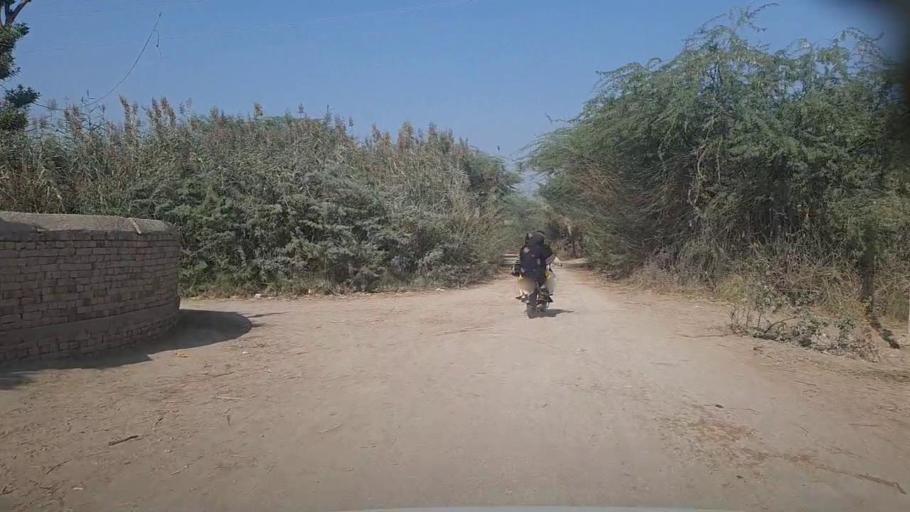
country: PK
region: Sindh
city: Karaundi
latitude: 26.9773
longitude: 68.4501
